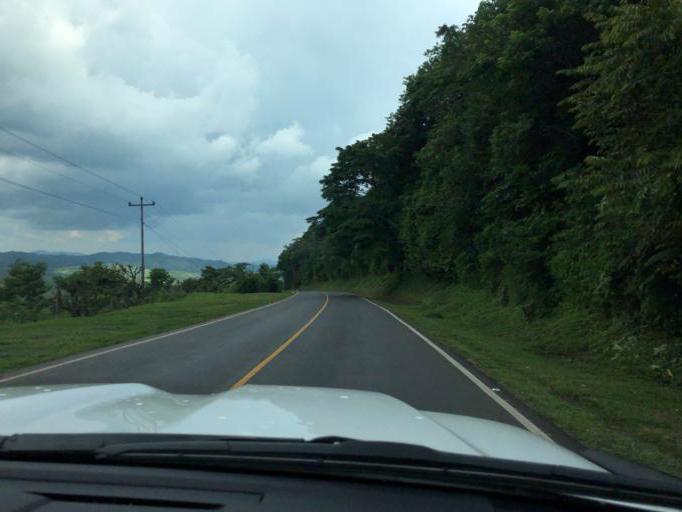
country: NI
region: Chontales
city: Villa Sandino
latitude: 12.0005
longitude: -84.7754
